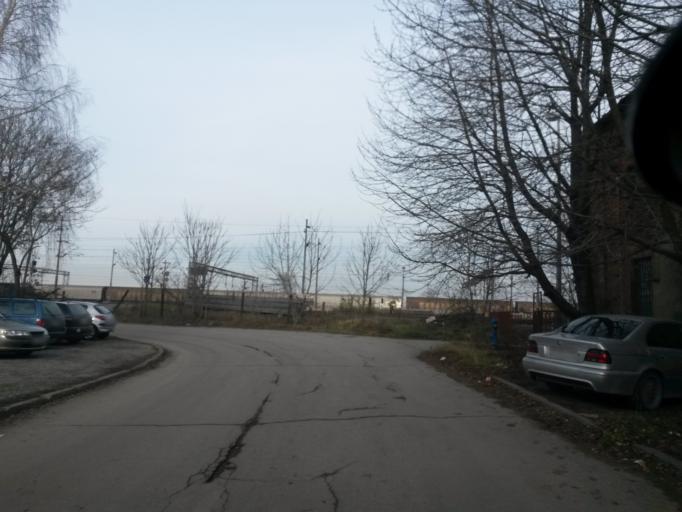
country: HR
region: Vukovarsko-Srijemska
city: Vinkovci
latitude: 45.2992
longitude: 18.8003
